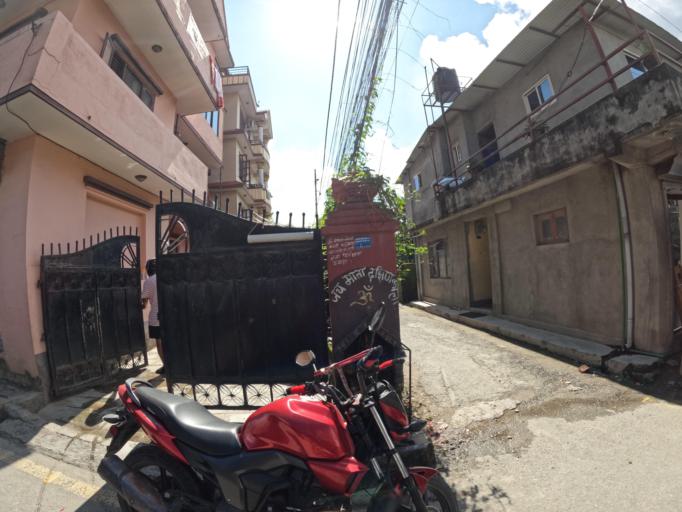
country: NP
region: Central Region
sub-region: Bagmati Zone
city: Kathmandu
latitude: 27.7517
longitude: 85.3336
